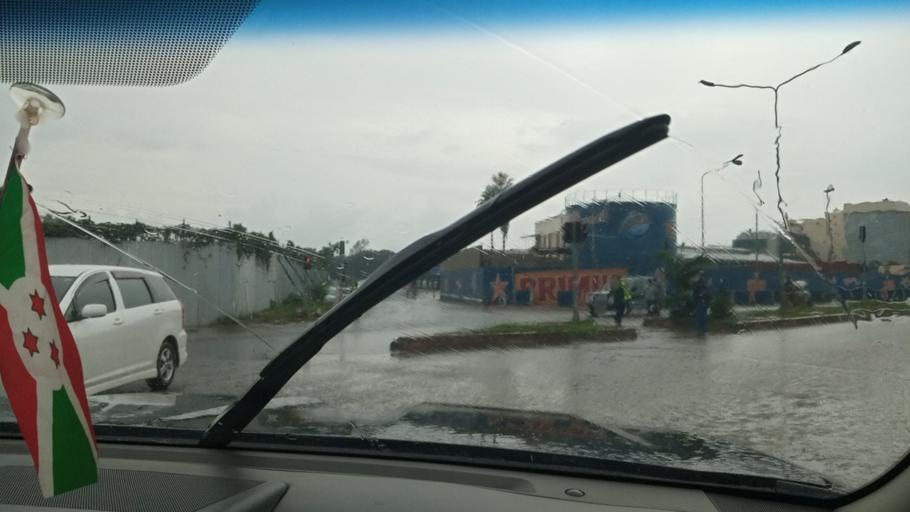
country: BI
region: Bujumbura Mairie
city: Bujumbura
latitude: -3.3739
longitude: 29.3499
